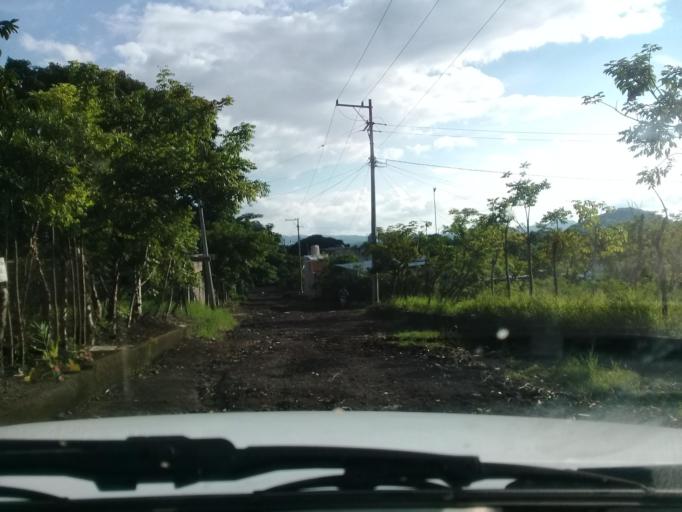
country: MX
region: Veracruz
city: Catemaco
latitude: 18.4319
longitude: -95.1090
